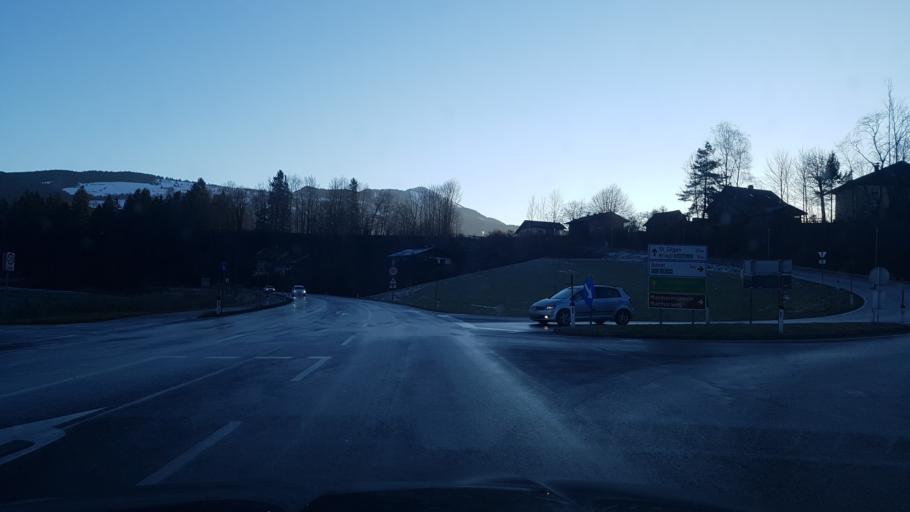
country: AT
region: Salzburg
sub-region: Politischer Bezirk Hallein
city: Oberalm
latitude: 47.6993
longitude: 13.1173
